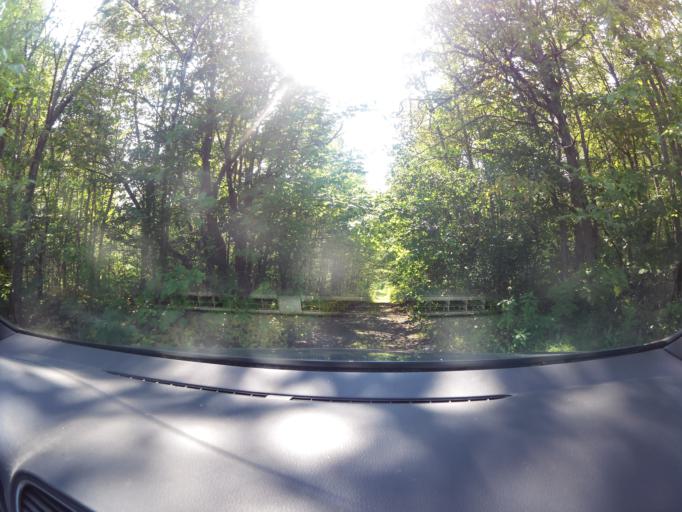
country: CA
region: Ontario
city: Carleton Place
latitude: 45.2728
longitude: -76.1430
